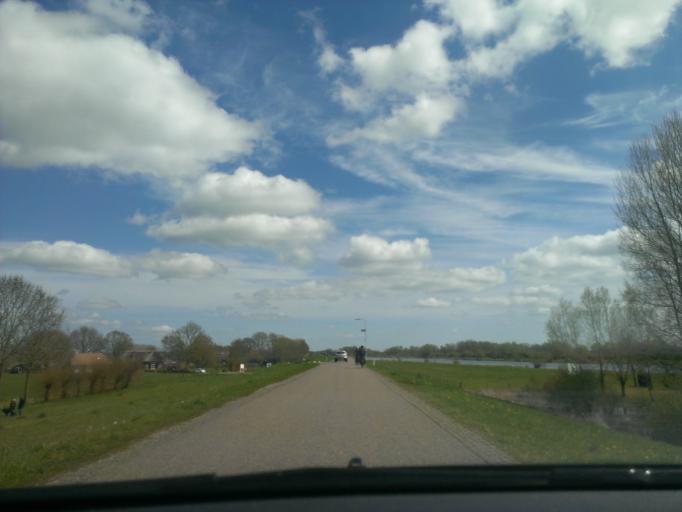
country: NL
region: Overijssel
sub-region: Gemeente Olst-Wijhe
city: Wijhe
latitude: 52.3766
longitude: 6.0986
